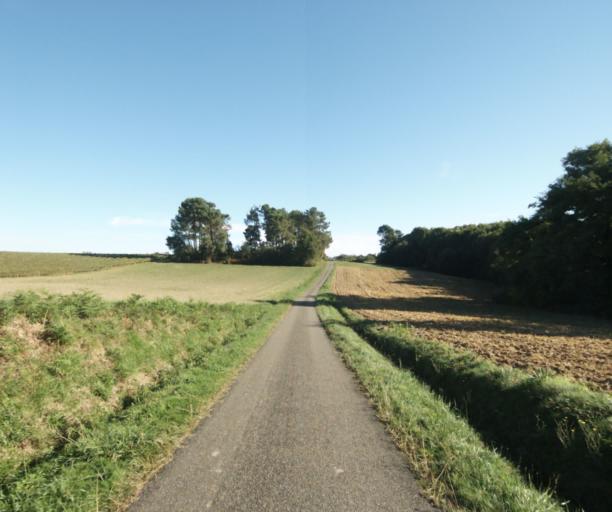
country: FR
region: Midi-Pyrenees
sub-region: Departement du Gers
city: Cazaubon
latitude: 43.8405
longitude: -0.0869
